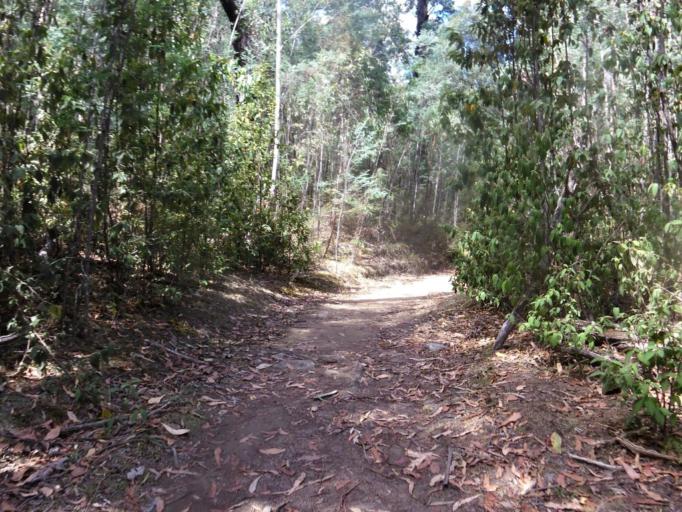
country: AU
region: Victoria
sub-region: Yarra Ranges
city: Healesville
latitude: -37.4124
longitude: 145.5645
